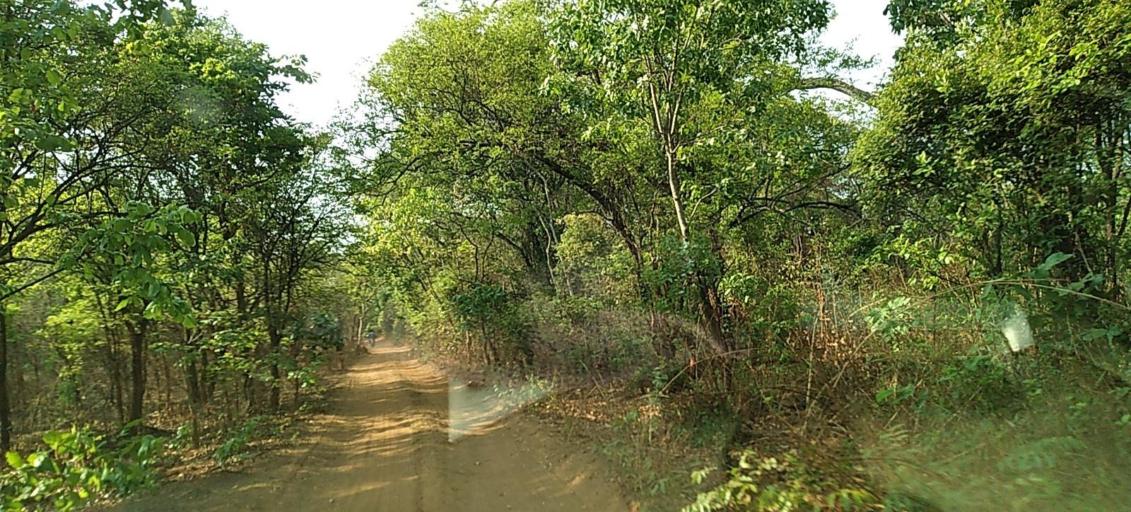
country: ZM
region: Copperbelt
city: Kalulushi
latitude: -12.9644
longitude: 27.7122
